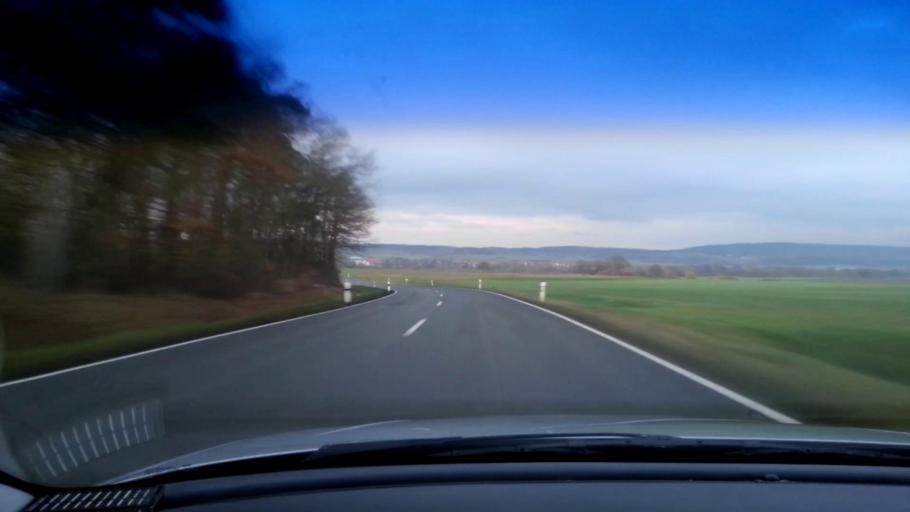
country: DE
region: Bavaria
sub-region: Upper Franconia
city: Frensdorf
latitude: 49.8142
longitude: 10.8410
